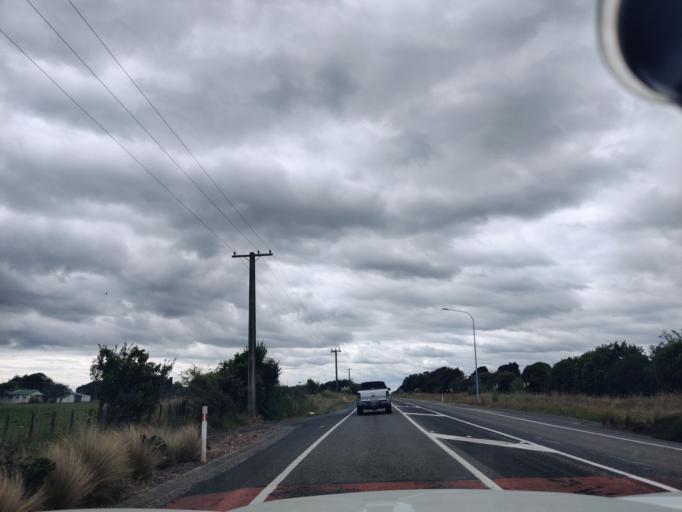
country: NZ
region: Wellington
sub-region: Kapiti Coast District
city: Otaki
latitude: -40.7089
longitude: 175.2187
